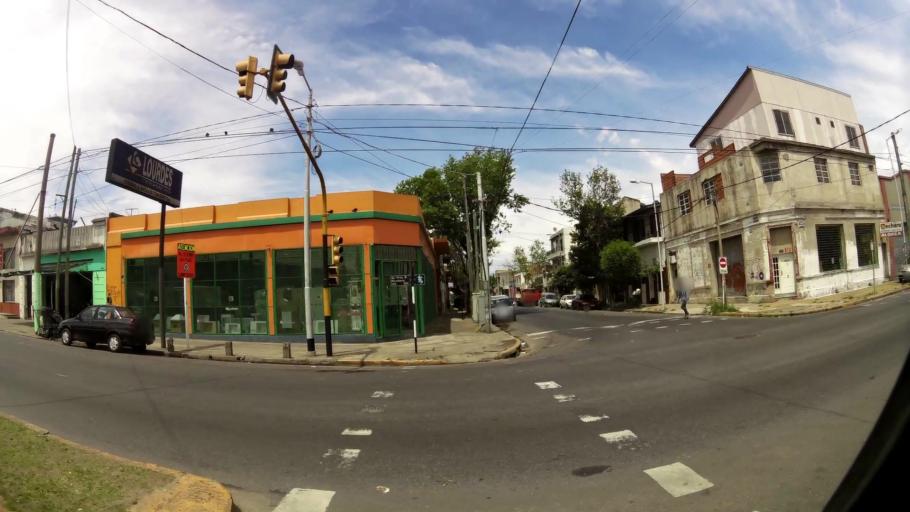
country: AR
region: Buenos Aires
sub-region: Partido de Avellaneda
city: Avellaneda
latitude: -34.6696
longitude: -58.3898
